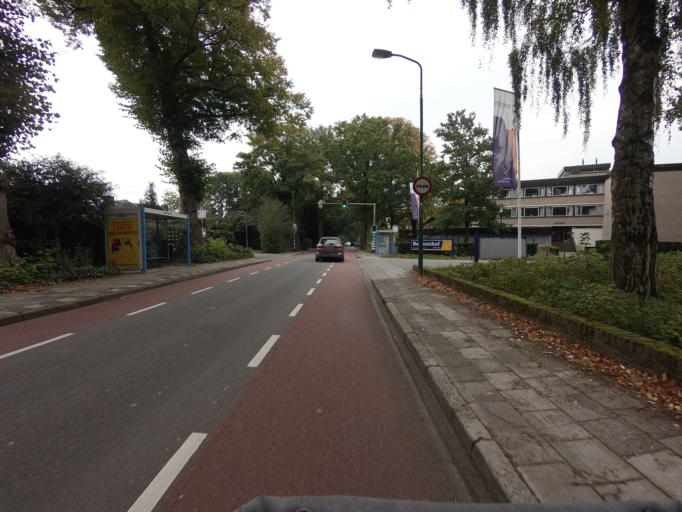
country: NL
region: North Holland
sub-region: Gemeente Wijdemeren
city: Nieuw-Loosdrecht
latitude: 52.2019
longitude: 5.1326
